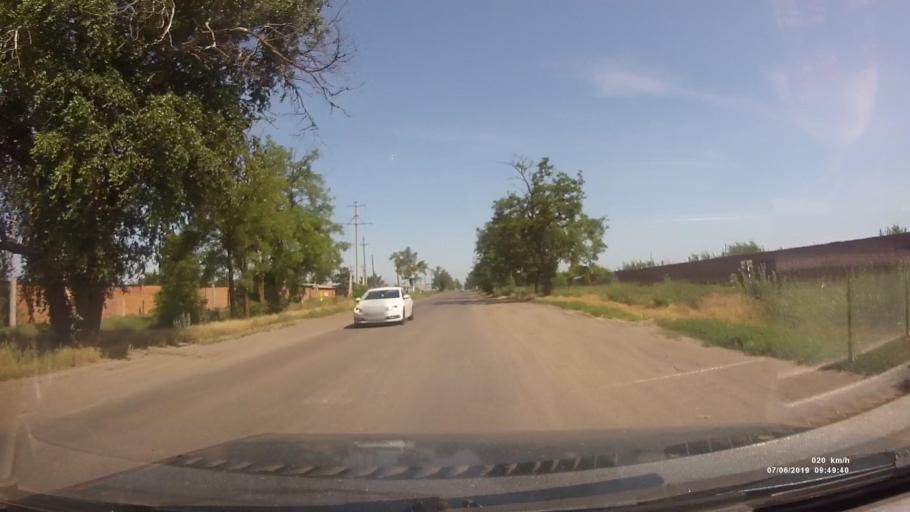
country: RU
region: Rostov
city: Azov
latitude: 47.0731
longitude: 39.4379
